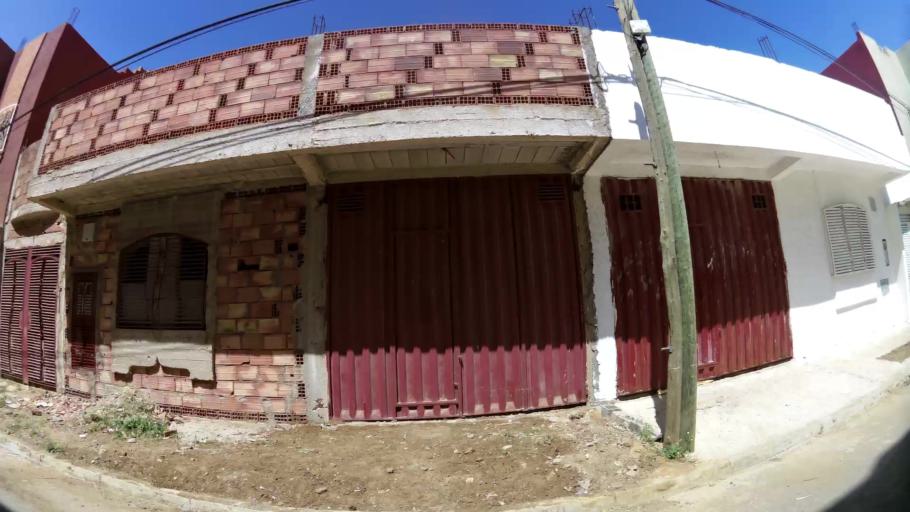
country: MA
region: Rabat-Sale-Zemmour-Zaer
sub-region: Khemisset
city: Khemisset
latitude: 33.8111
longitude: -6.0900
